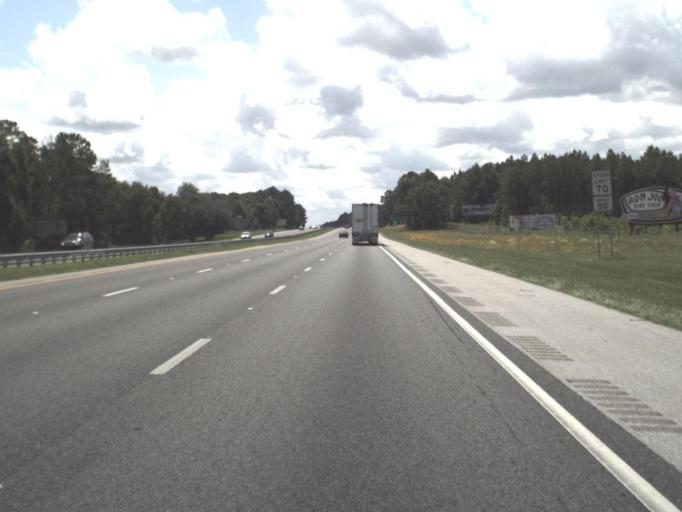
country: US
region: Florida
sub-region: Suwannee County
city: Wellborn
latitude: 30.3111
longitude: -82.8008
